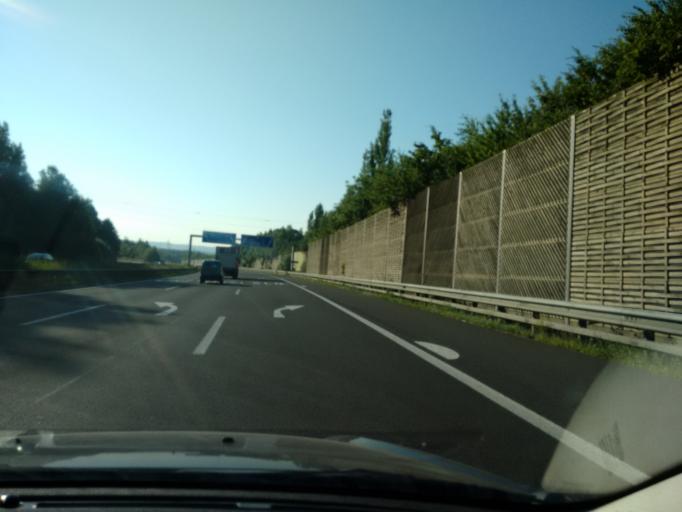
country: AT
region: Upper Austria
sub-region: Wels Stadt
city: Wels
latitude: 48.1811
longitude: 13.9796
